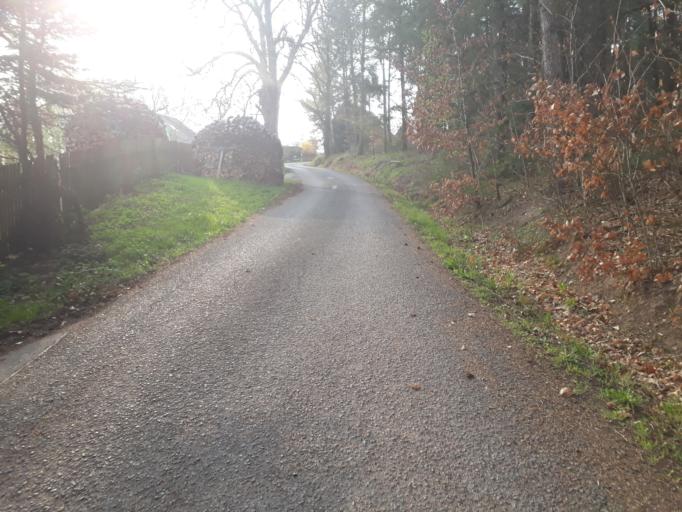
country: DE
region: Saxony
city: Reinhardtsgrimma
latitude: 50.8918
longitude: 13.7776
